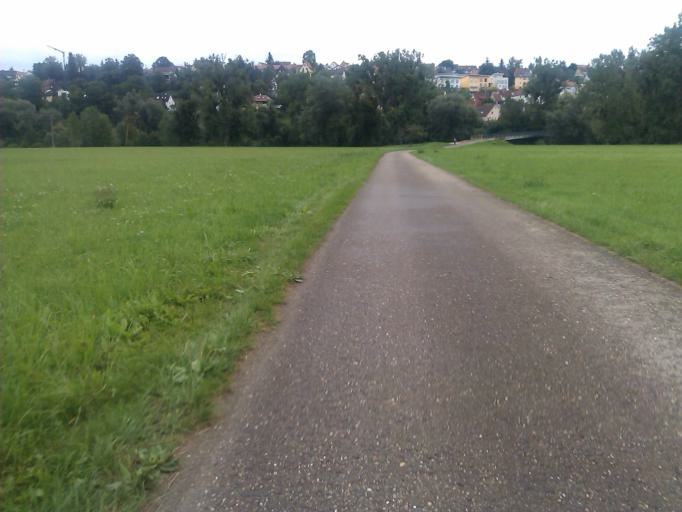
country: DE
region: Baden-Wuerttemberg
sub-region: Tuebingen Region
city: Kirchentellinsfurt
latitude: 48.5354
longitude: 9.1393
